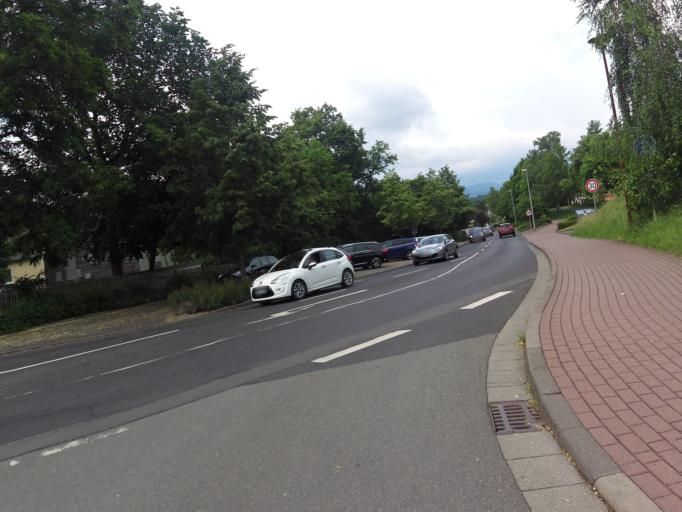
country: DE
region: Thuringia
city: Bad Salzungen
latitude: 50.8065
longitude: 10.2383
